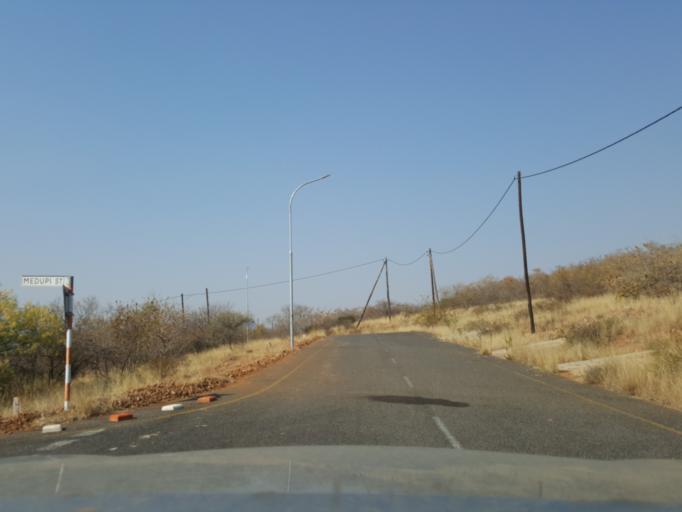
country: BW
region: South East
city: Lobatse
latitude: -25.1796
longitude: 25.6800
